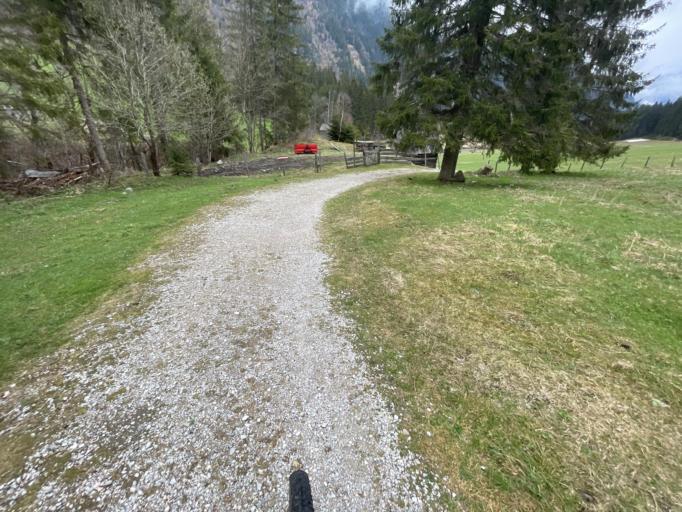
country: AT
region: Styria
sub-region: Politischer Bezirk Liezen
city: Schladming
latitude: 47.3543
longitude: 13.7115
